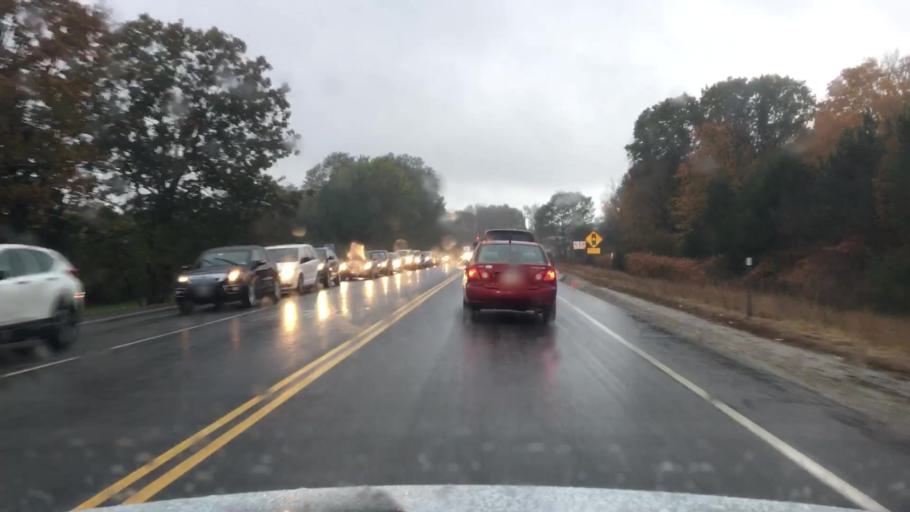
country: US
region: New Hampshire
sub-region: Strafford County
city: Rochester
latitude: 43.2778
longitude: -70.9809
